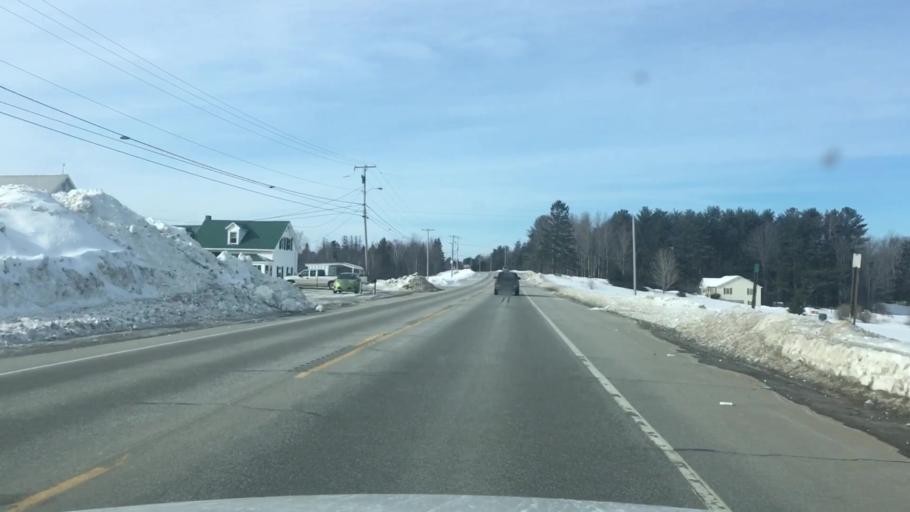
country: US
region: Maine
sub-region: Penobscot County
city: Kenduskeag
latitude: 44.9519
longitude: -68.9486
